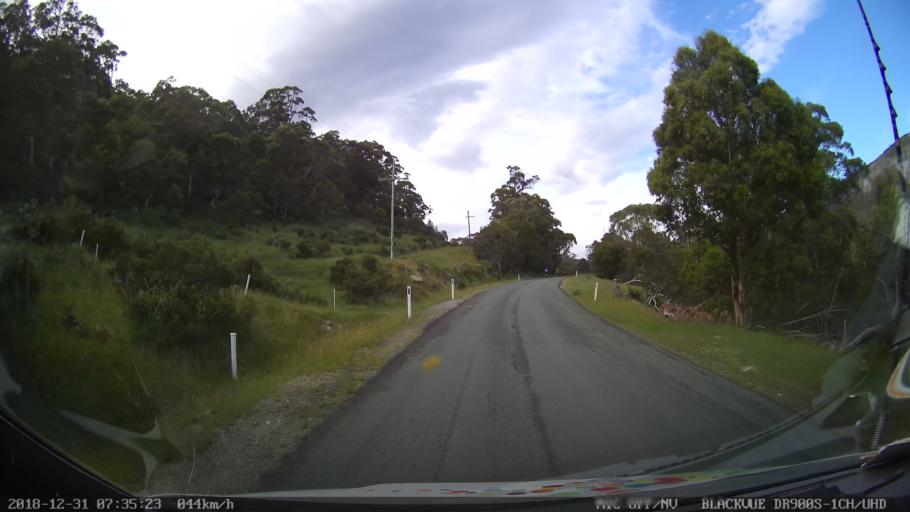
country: AU
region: New South Wales
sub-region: Snowy River
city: Jindabyne
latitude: -36.3347
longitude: 148.4451
